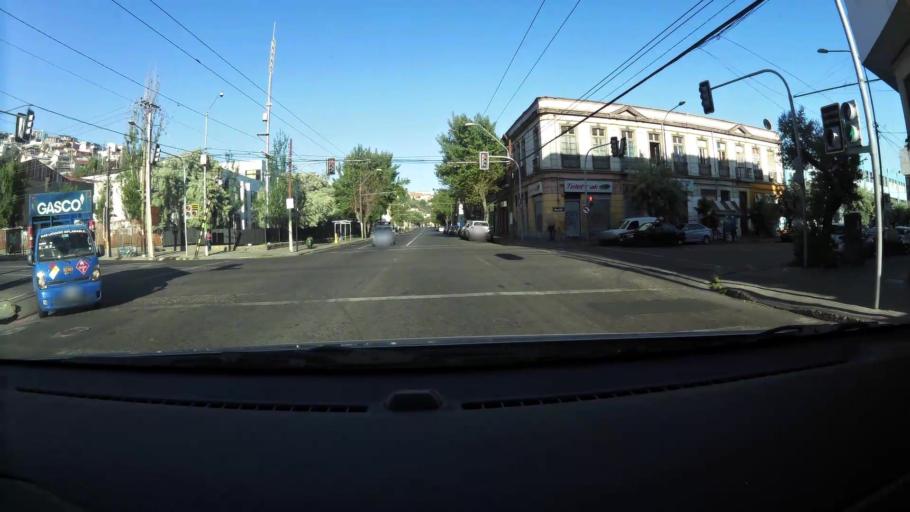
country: CL
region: Valparaiso
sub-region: Provincia de Valparaiso
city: Valparaiso
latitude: -33.0498
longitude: -71.6127
